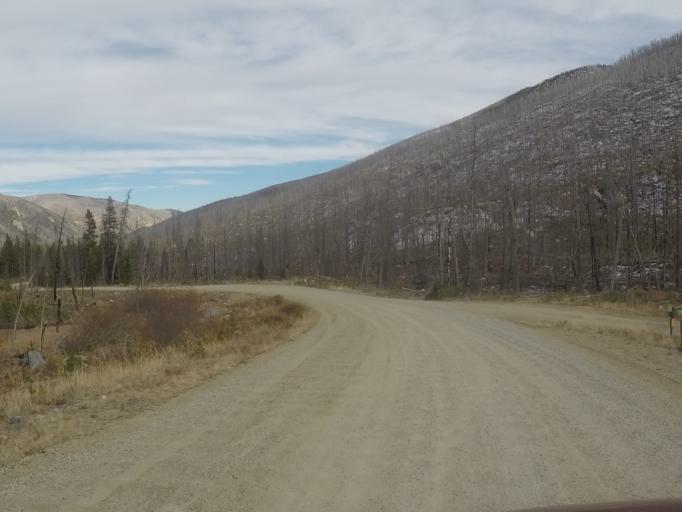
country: US
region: Montana
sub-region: Carbon County
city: Red Lodge
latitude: 45.1720
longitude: -109.4719
